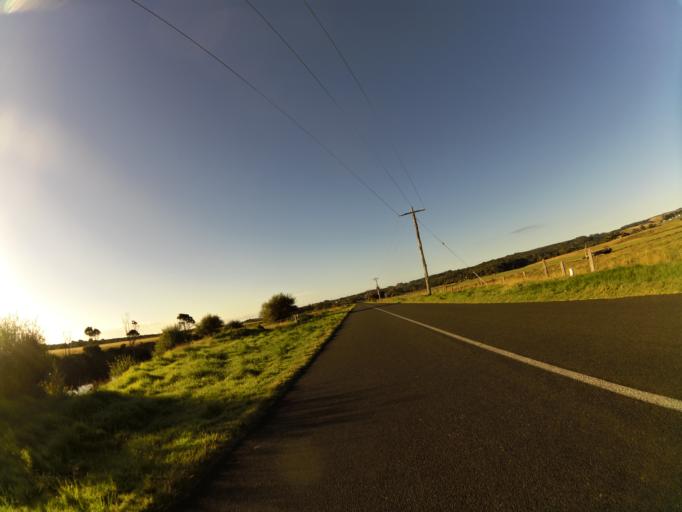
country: AU
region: Victoria
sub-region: Colac-Otway
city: Apollo Bay
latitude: -38.7625
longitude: 143.6618
